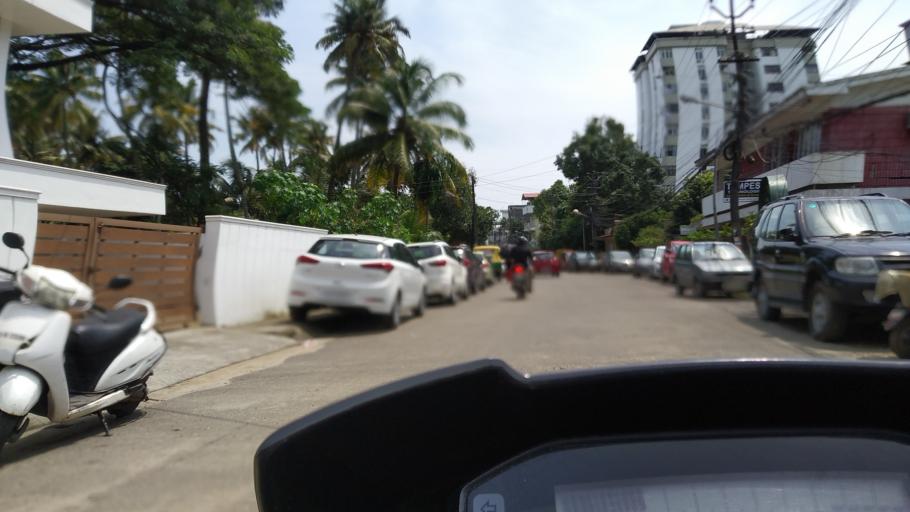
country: IN
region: Kerala
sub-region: Ernakulam
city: Cochin
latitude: 9.9573
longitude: 76.2924
